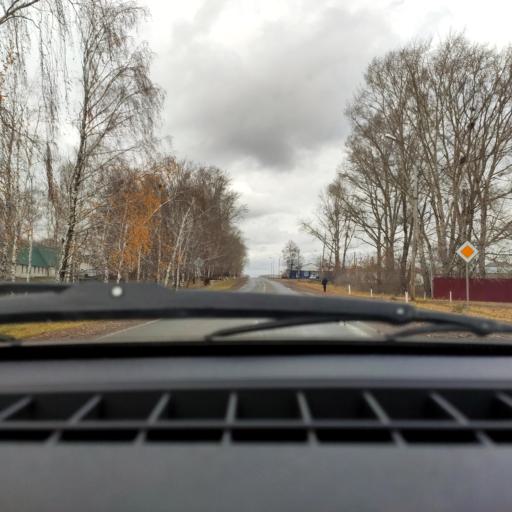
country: RU
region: Bashkortostan
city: Asanovo
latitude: 54.9590
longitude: 55.5515
